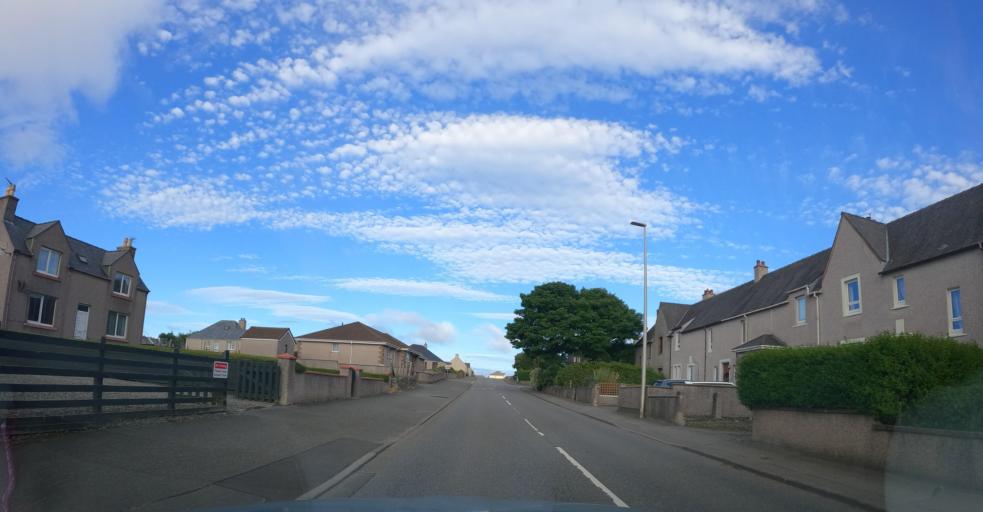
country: GB
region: Scotland
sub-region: Eilean Siar
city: Isle of Lewis
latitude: 58.2186
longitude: -6.3809
